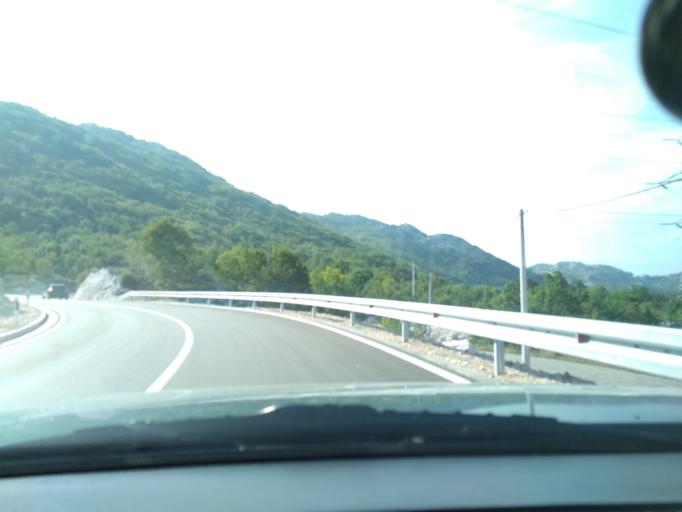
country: ME
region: Cetinje
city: Cetinje
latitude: 42.4145
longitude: 18.8823
